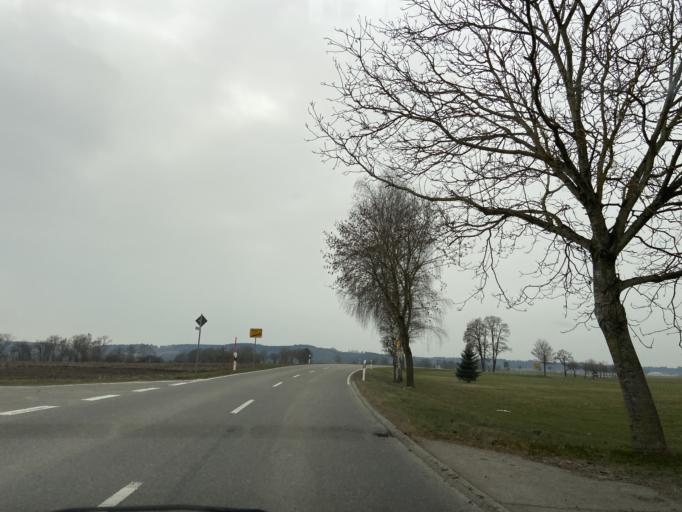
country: DE
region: Baden-Wuerttemberg
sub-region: Tuebingen Region
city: Ostrach
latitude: 47.9290
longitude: 9.3548
